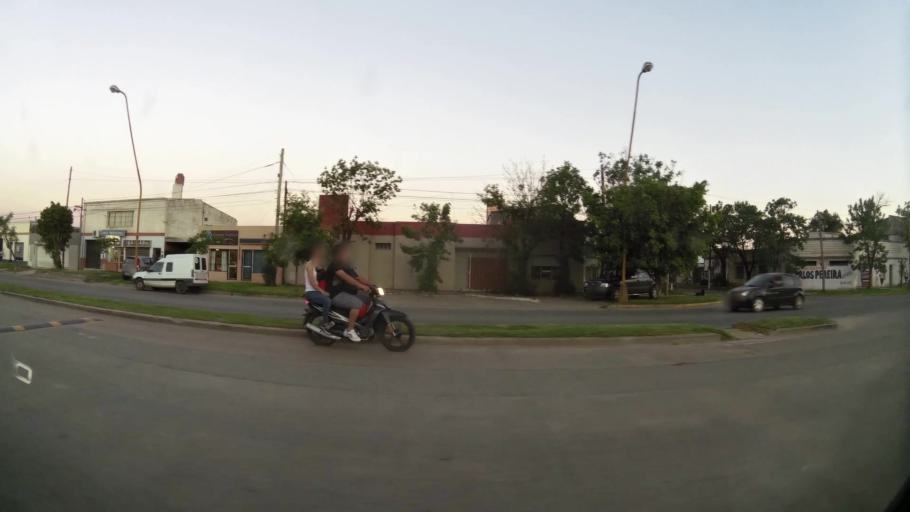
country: AR
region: Santa Fe
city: Santa Fe de la Vera Cruz
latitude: -31.6009
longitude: -60.7018
